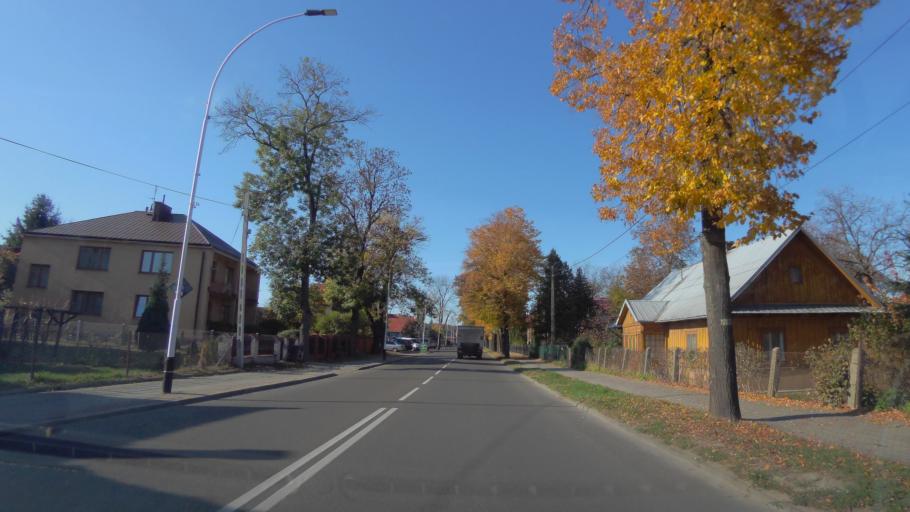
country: PL
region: Subcarpathian Voivodeship
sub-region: Powiat lezajski
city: Lezajsk
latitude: 50.2651
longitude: 22.4141
